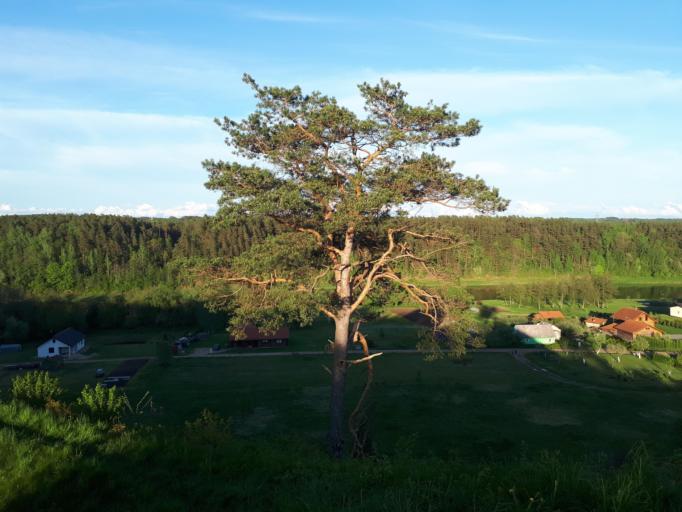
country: LT
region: Alytaus apskritis
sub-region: Alytus
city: Alytus
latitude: 54.4725
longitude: 24.0519
